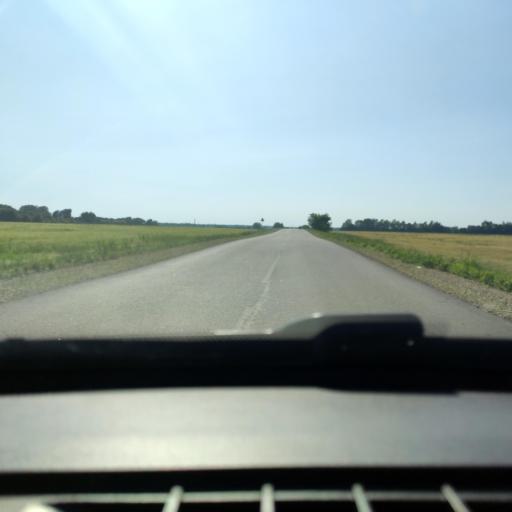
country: RU
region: Voronezj
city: Anna
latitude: 51.6283
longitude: 40.3413
